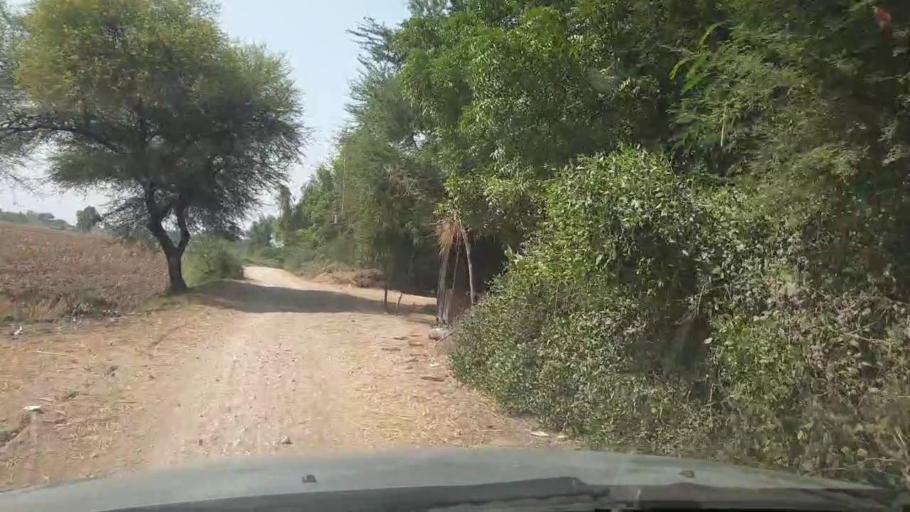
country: PK
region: Sindh
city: Bulri
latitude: 24.8725
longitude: 68.3168
